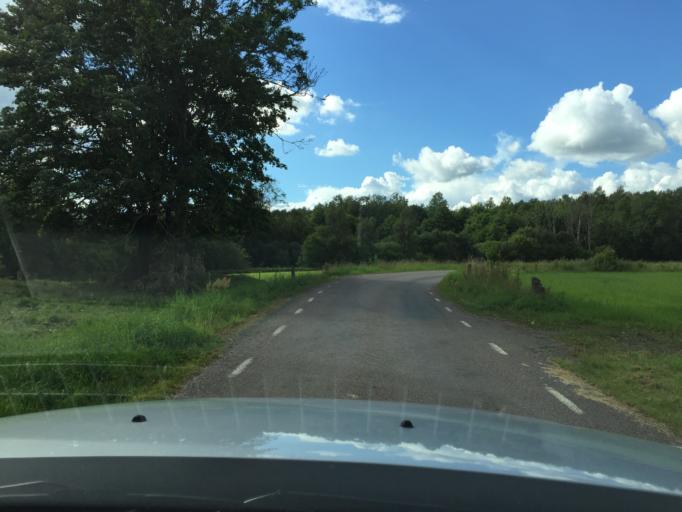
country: SE
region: Skane
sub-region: Hassleholms Kommun
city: Vinslov
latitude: 55.9745
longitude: 13.8451
